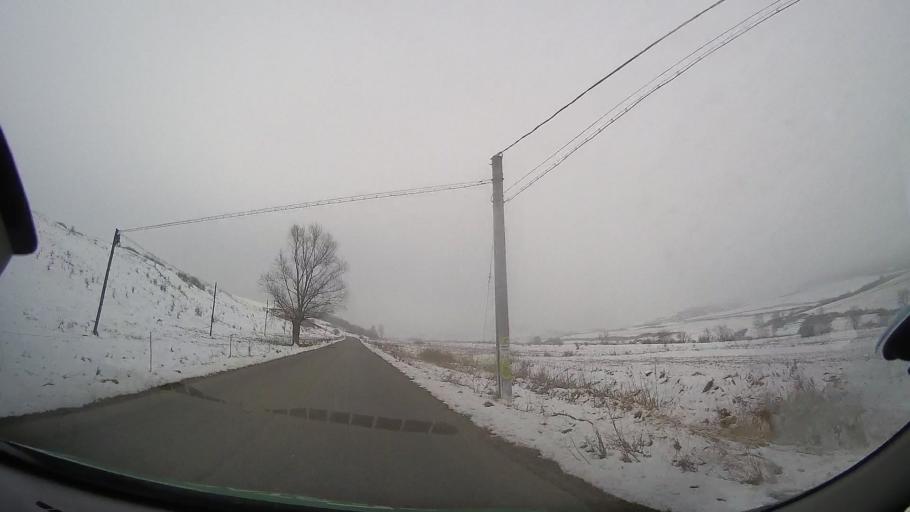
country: RO
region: Bacau
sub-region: Comuna Vultureni
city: Vultureni
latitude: 46.3176
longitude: 27.2929
